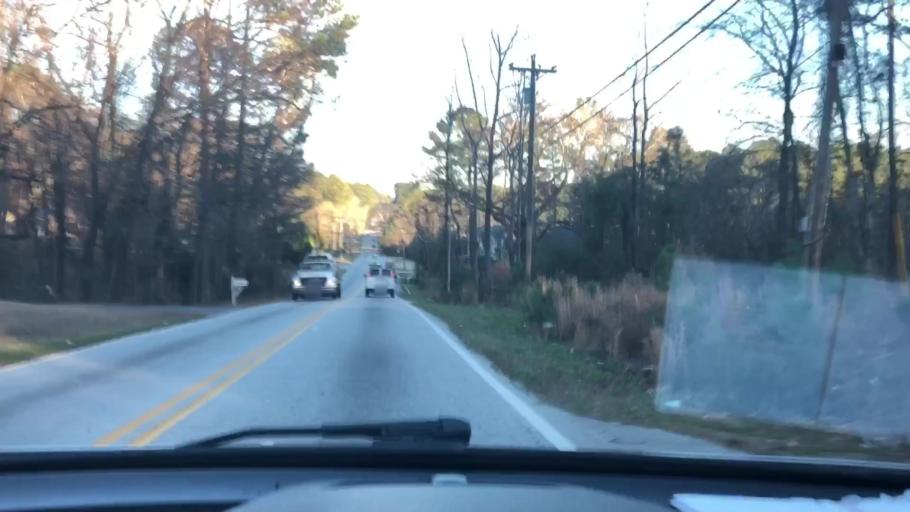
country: US
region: Georgia
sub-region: DeKalb County
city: Lithonia
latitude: 33.7347
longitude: -84.0843
